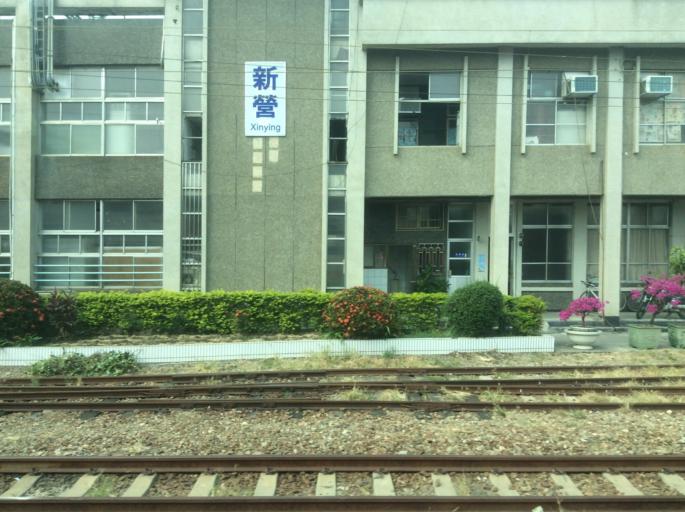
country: TW
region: Taiwan
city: Xinying
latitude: 23.3069
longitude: 120.3233
